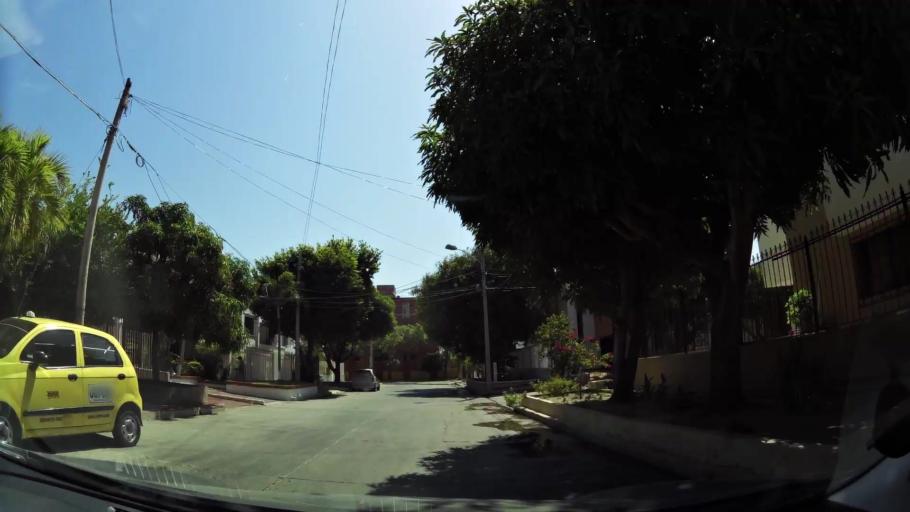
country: CO
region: Atlantico
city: Barranquilla
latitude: 11.0094
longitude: -74.7937
